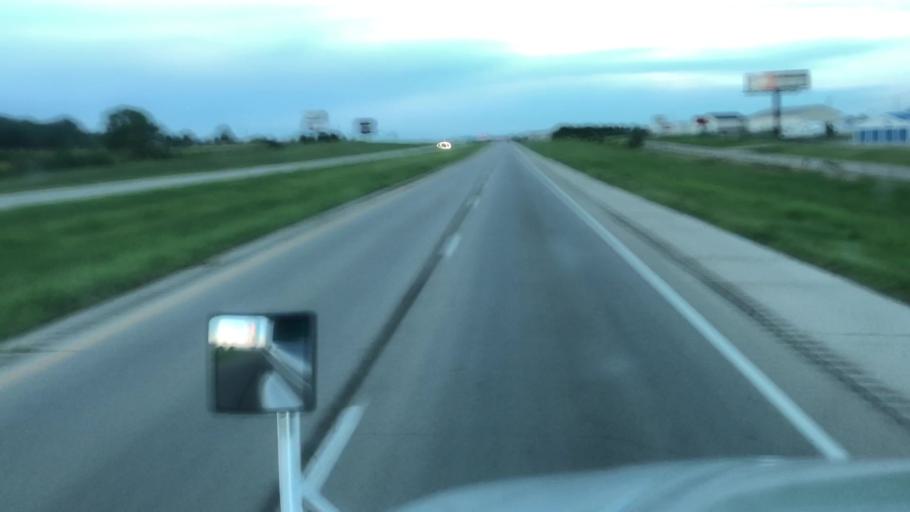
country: US
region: Oklahoma
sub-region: Kay County
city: Ponca City
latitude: 36.7567
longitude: -97.0648
